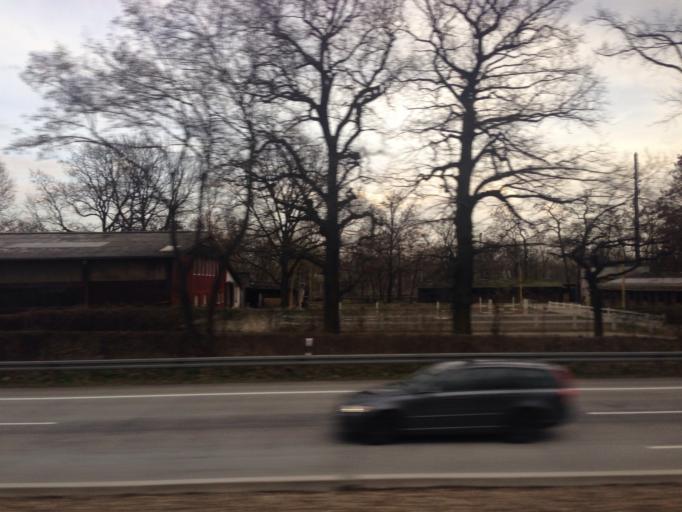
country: DE
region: Berlin
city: Grunewald
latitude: 52.4903
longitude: 13.2619
